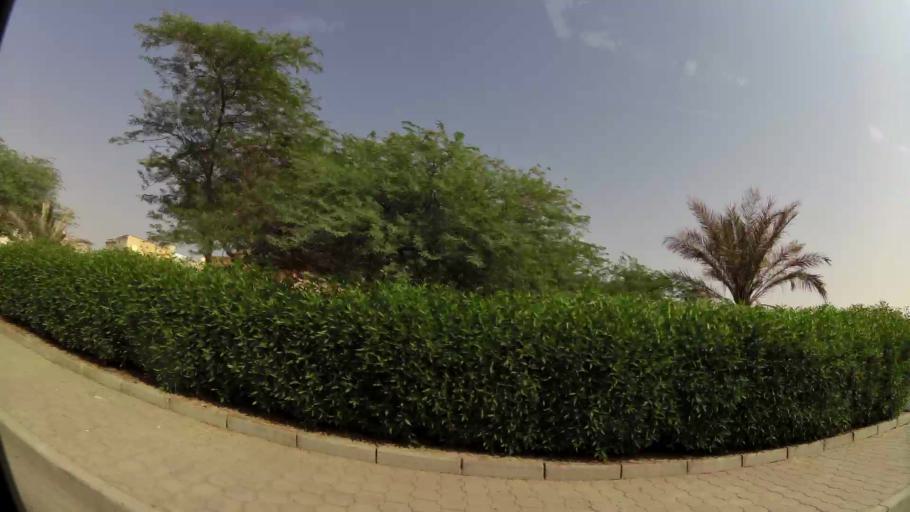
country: KW
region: Muhafazat al Jahra'
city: Al Jahra'
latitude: 29.3275
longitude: 47.6473
